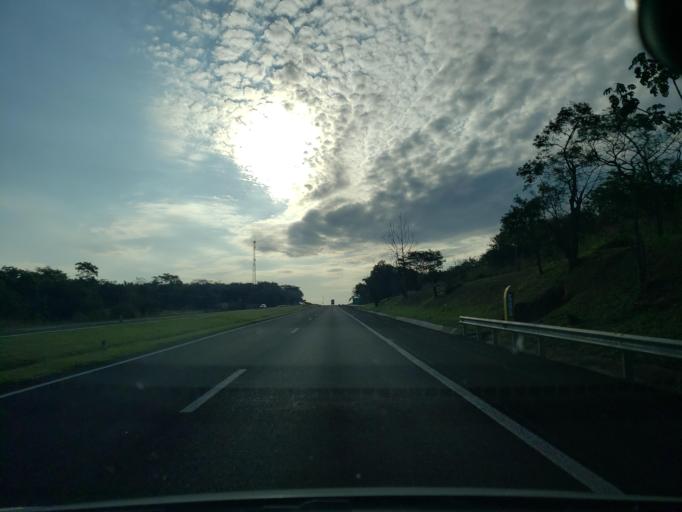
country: BR
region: Sao Paulo
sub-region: Valparaiso
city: Valparaiso
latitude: -21.1748
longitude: -50.9283
